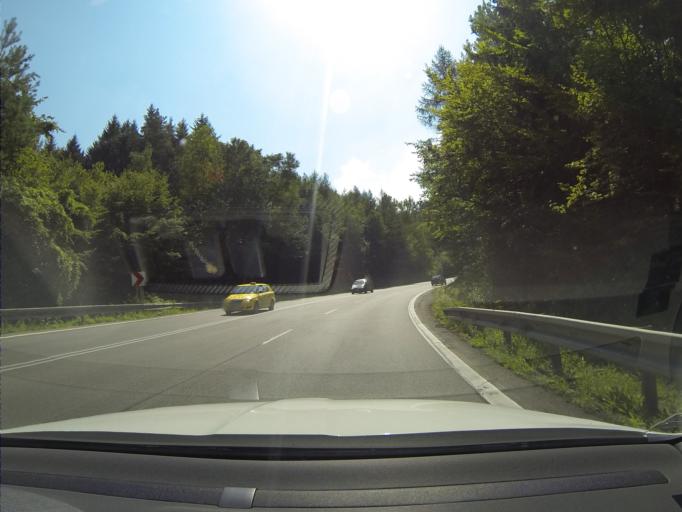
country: SK
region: Nitriansky
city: Prievidza
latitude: 48.7767
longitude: 18.6749
